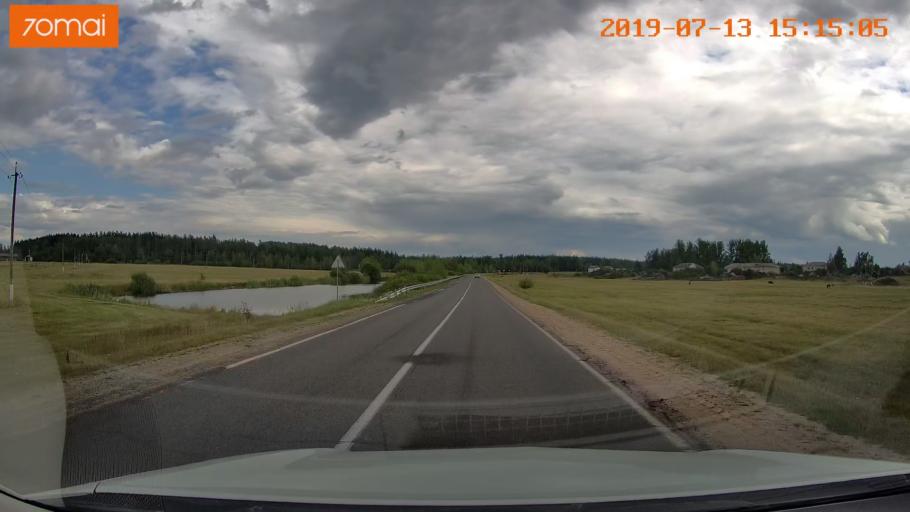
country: BY
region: Mogilev
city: Hlusha
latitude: 53.1193
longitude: 28.8221
